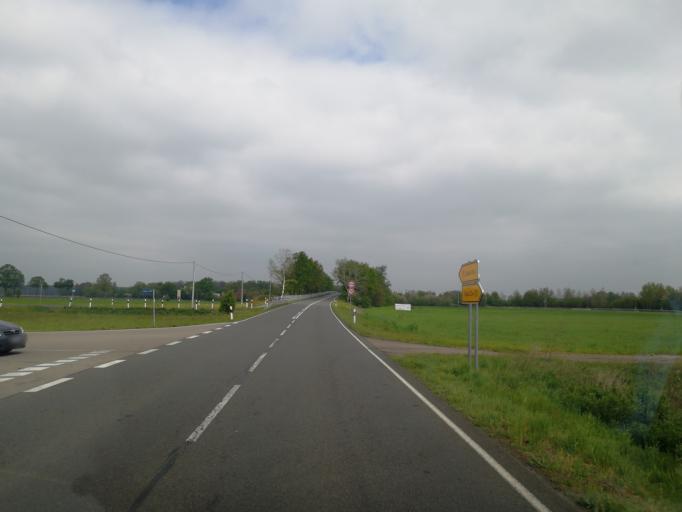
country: DE
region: Brandenburg
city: Herzberg
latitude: 51.6729
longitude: 13.2024
